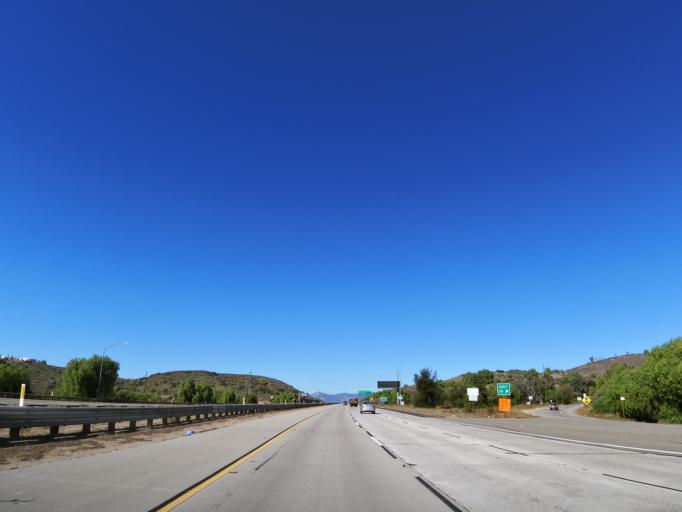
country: US
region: California
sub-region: Ventura County
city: Moorpark
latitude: 34.2643
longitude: -118.8491
